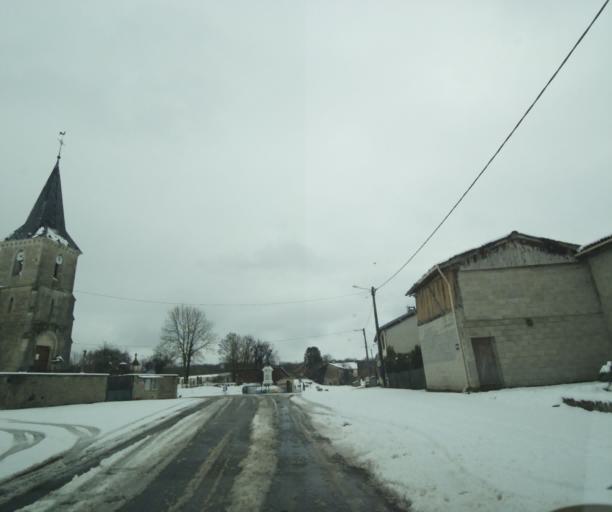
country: FR
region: Champagne-Ardenne
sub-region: Departement de la Haute-Marne
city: Montier-en-Der
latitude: 48.4128
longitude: 4.7376
